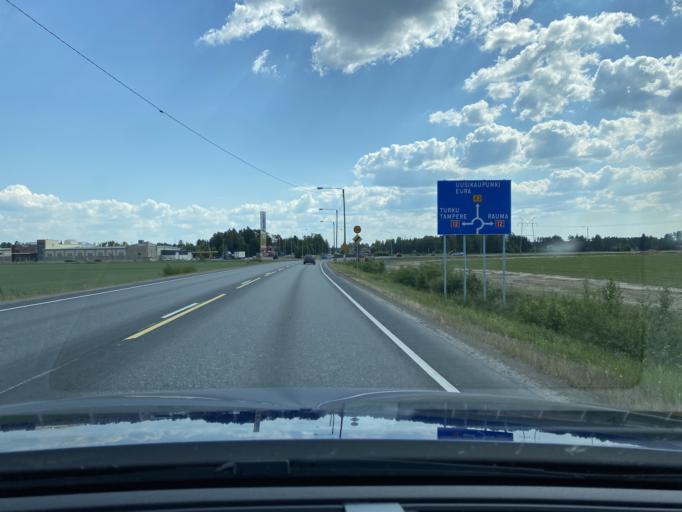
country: FI
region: Satakunta
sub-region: Rauma
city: Eura
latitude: 61.1333
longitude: 22.1231
